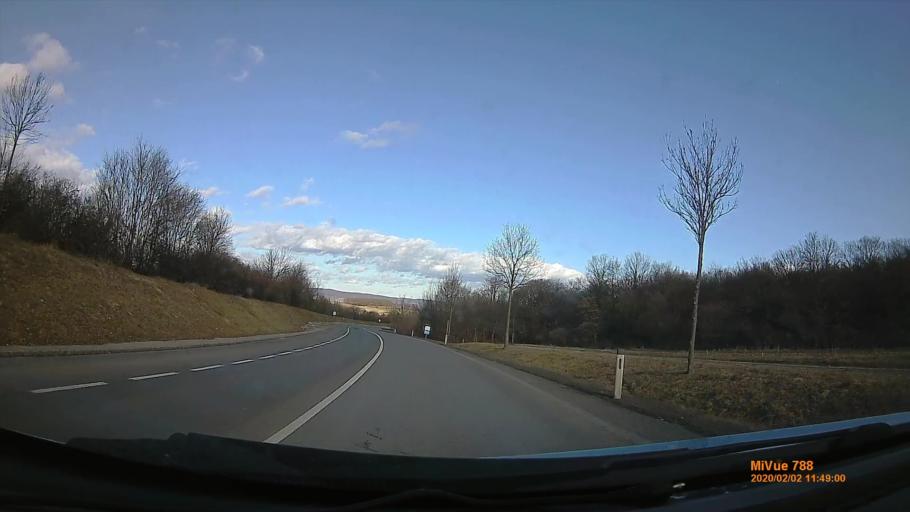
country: AT
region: Burgenland
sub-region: Eisenstadt-Umgebung
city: Klingenbach
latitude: 47.7478
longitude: 16.5451
